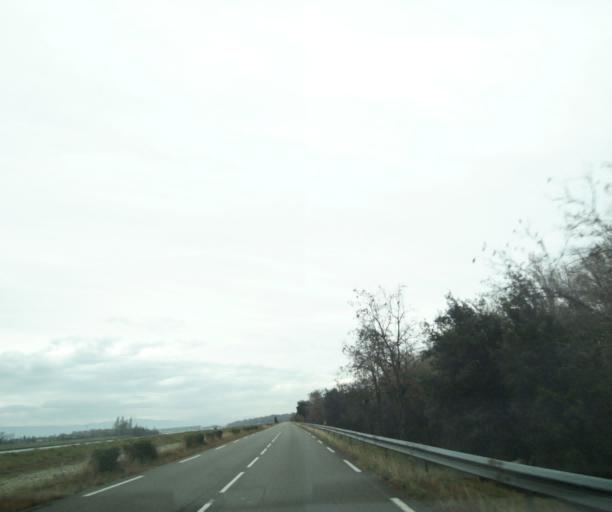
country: FR
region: Rhone-Alpes
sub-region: Departement de l'Ardeche
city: Cornas
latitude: 44.9748
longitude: 4.8572
